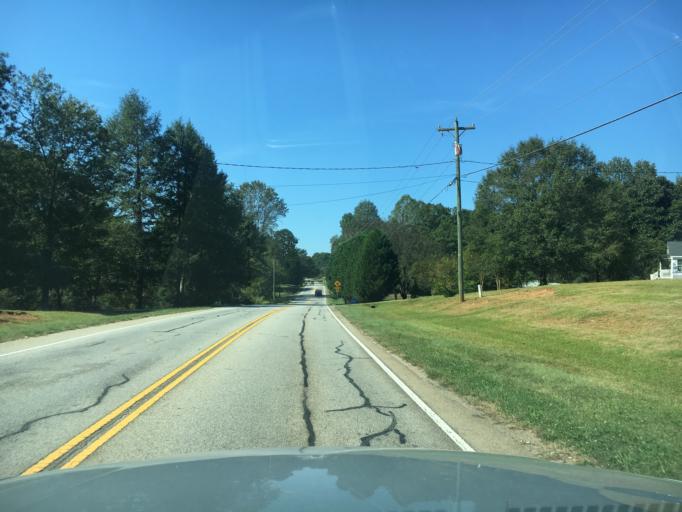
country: US
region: South Carolina
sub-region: Greenville County
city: Taylors
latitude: 34.9055
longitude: -82.2779
